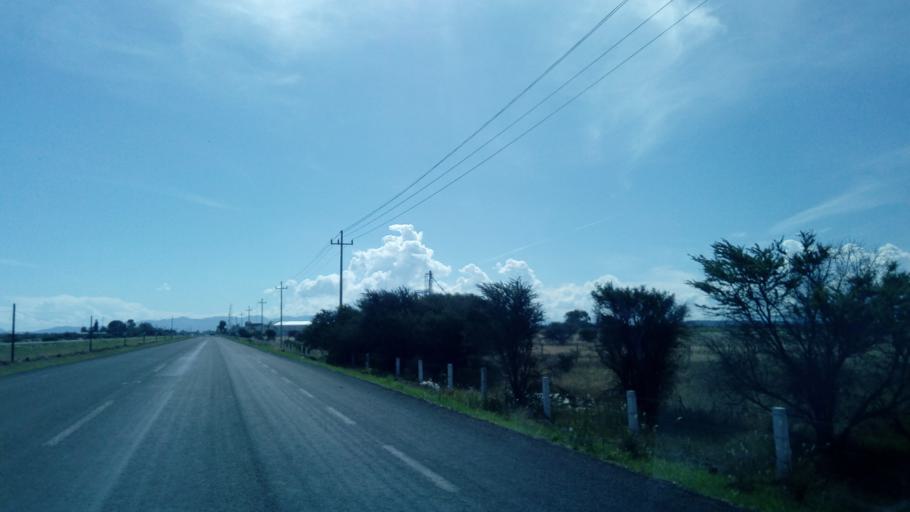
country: MX
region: Durango
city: Victoria de Durango
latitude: 24.0871
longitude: -104.5644
